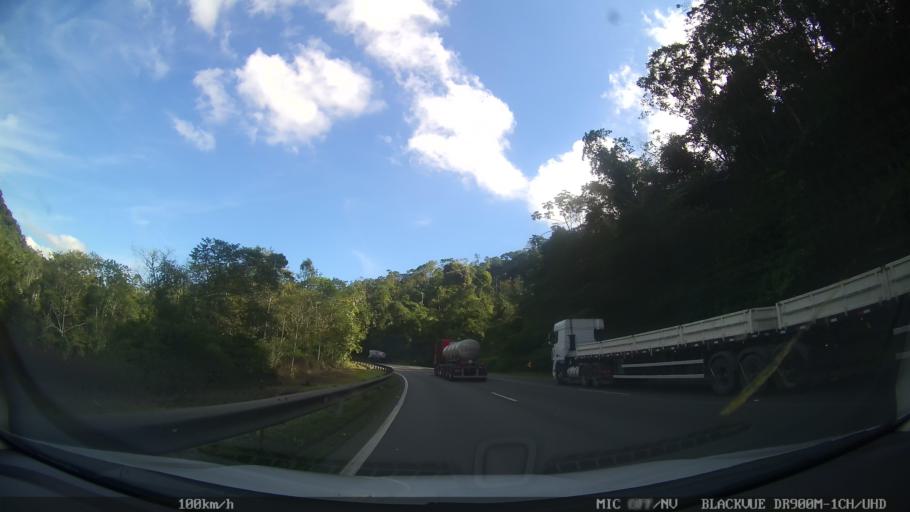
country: BR
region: Sao Paulo
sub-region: Cajati
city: Cajati
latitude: -24.8940
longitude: -48.2434
